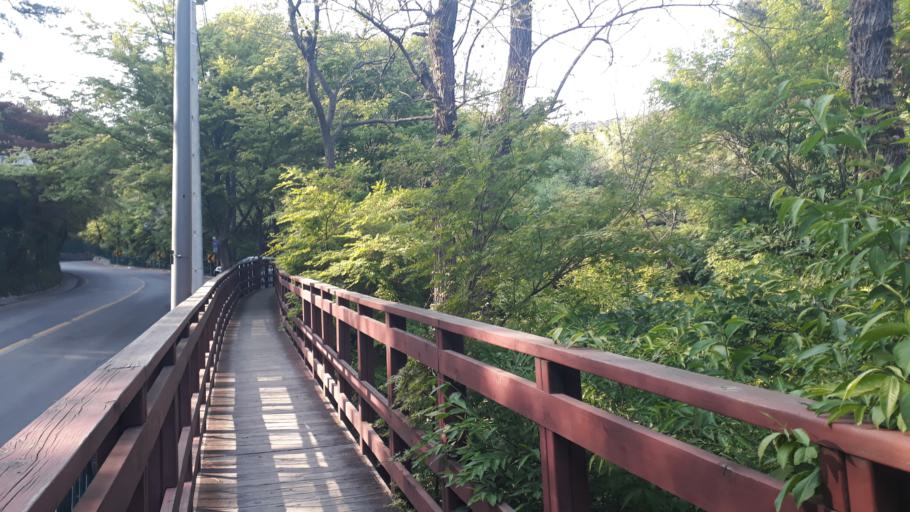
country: KR
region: Seoul
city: Seoul
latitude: 37.5892
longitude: 126.9831
